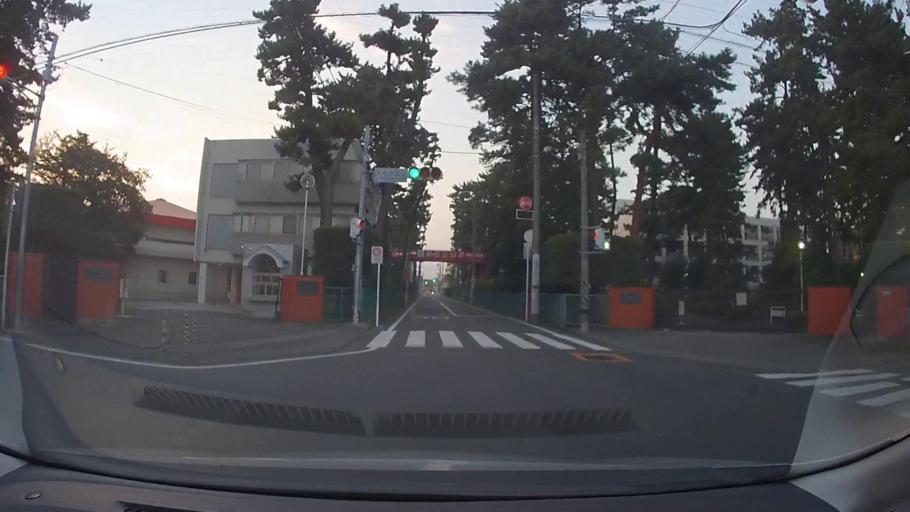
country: JP
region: Kanagawa
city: Minami-rinkan
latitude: 35.4991
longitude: 139.4449
